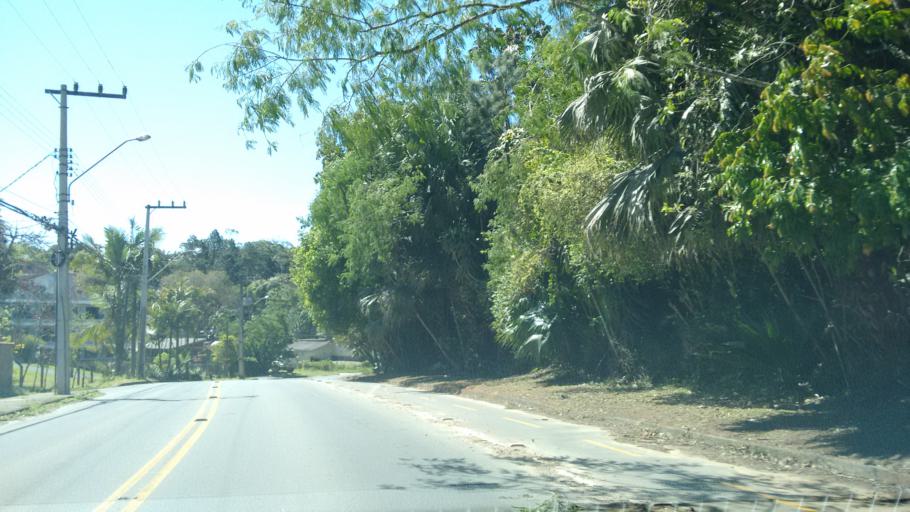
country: BR
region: Santa Catarina
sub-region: Blumenau
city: Blumenau
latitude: -26.8880
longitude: -49.1255
